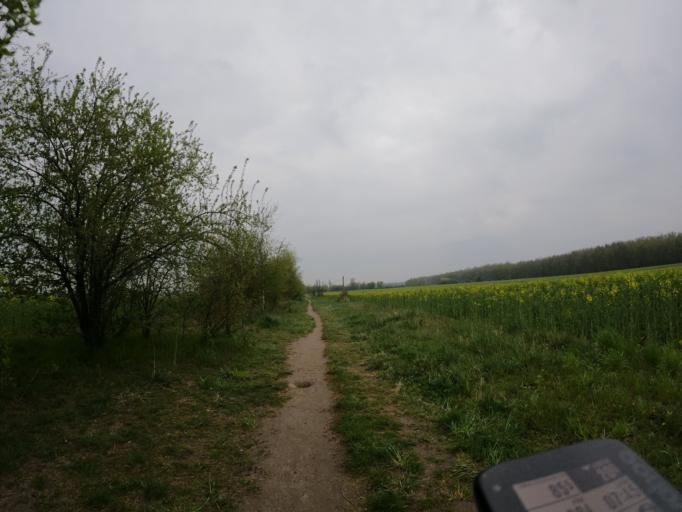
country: DE
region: Berlin
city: Lichtenrade
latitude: 52.3929
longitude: 13.4294
